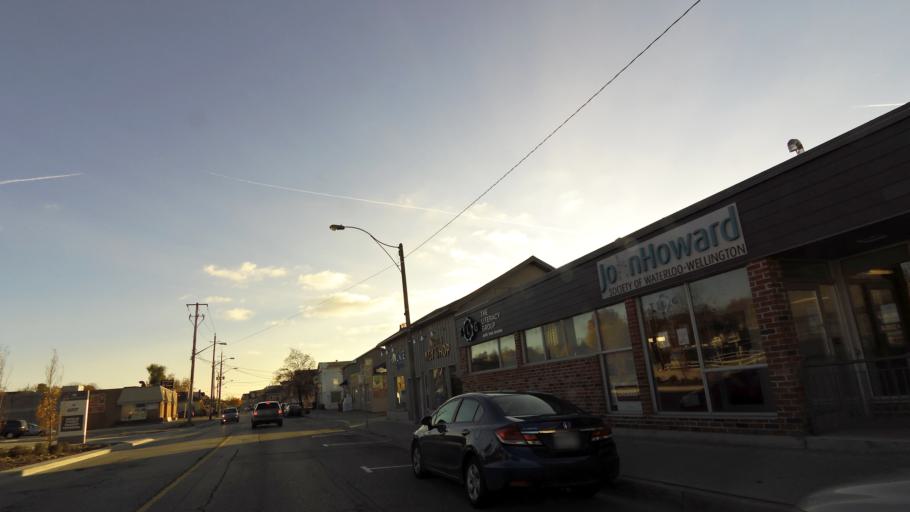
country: CA
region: Ontario
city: Cambridge
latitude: 43.3573
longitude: -80.3136
